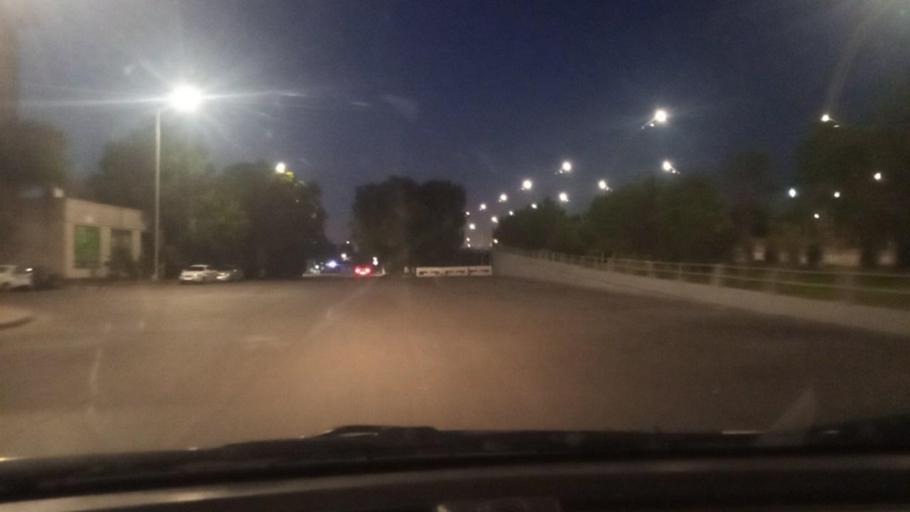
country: UZ
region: Toshkent Shahri
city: Tashkent
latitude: 41.2707
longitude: 69.2605
